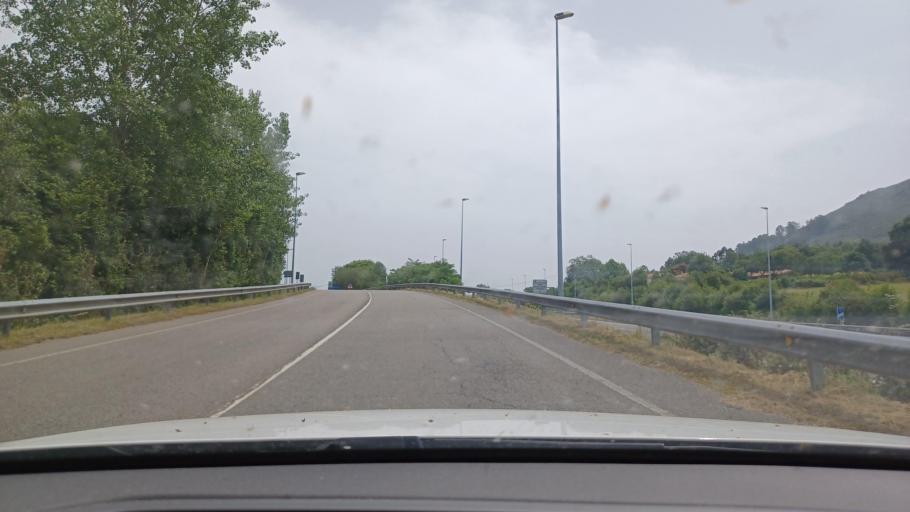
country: ES
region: Asturias
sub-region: Province of Asturias
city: Ribadesella
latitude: 43.4395
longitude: -4.9649
